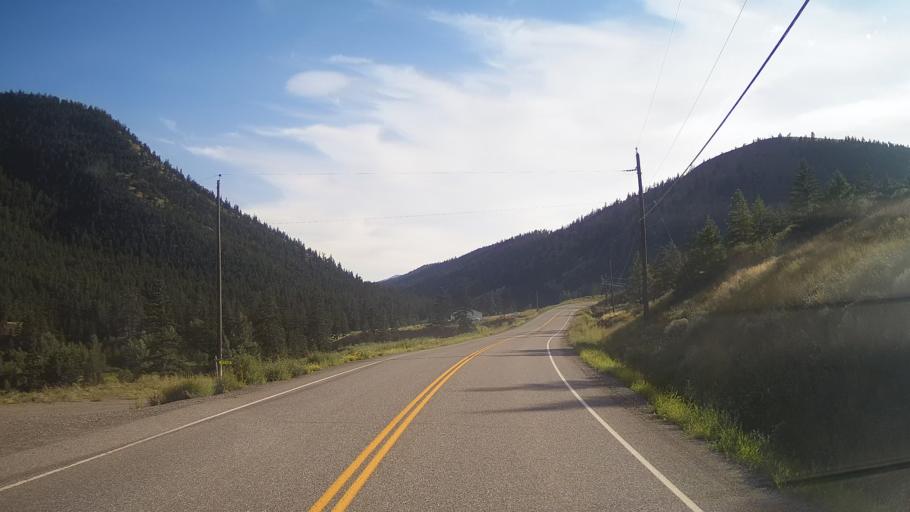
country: CA
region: British Columbia
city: Cache Creek
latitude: 50.8791
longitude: -121.5107
